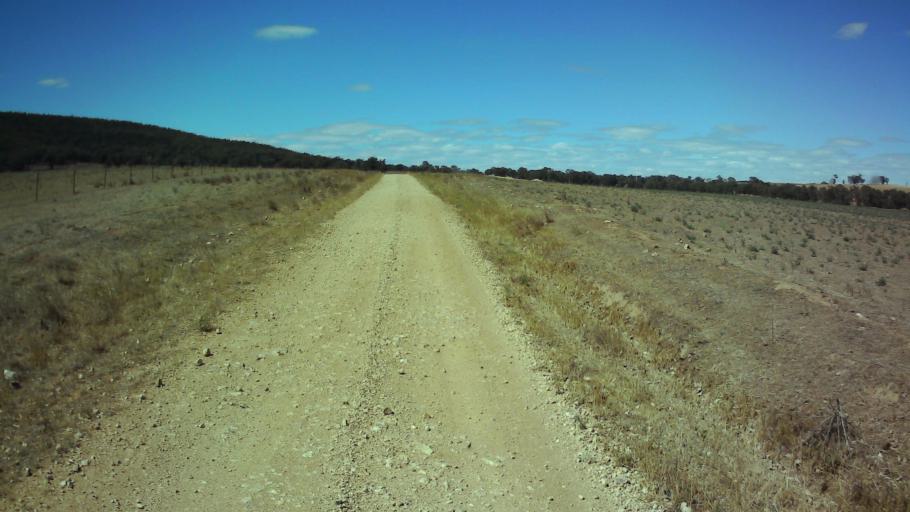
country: AU
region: New South Wales
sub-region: Weddin
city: Grenfell
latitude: -34.0364
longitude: 148.4337
